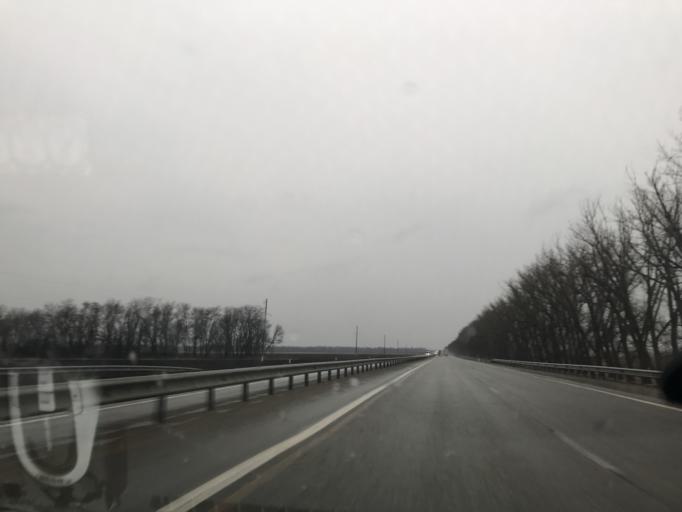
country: RU
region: Krasnodarskiy
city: Kislyakovskaya
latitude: 46.3796
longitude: 39.7470
